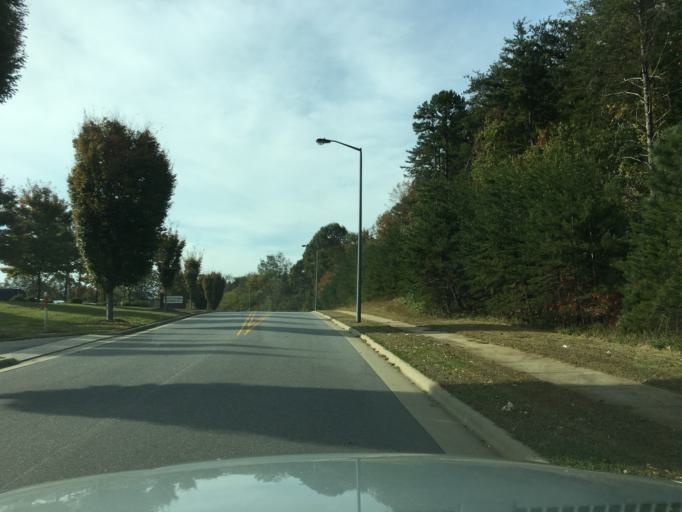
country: US
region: North Carolina
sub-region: Catawba County
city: Saint Stephens
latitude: 35.7305
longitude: -81.2882
